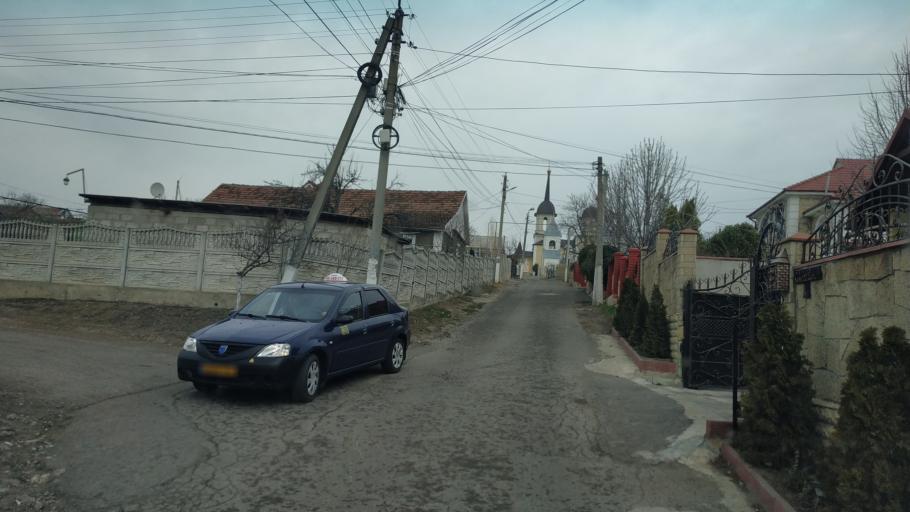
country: MD
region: Chisinau
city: Singera
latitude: 46.9352
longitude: 28.9920
